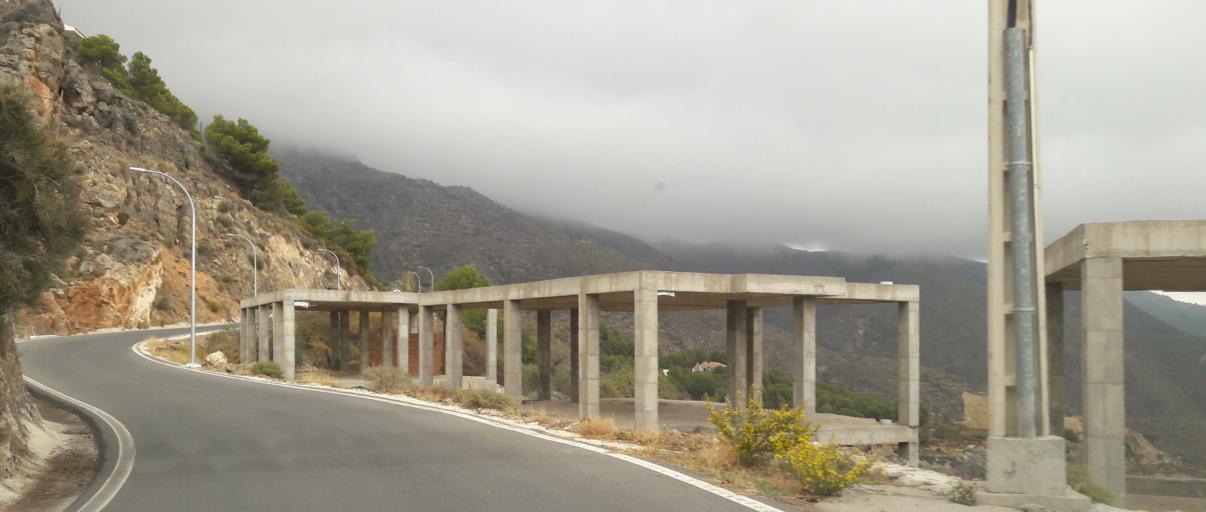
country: ES
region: Andalusia
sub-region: Provincia de Almeria
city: Vicar
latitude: 36.8691
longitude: -2.6546
